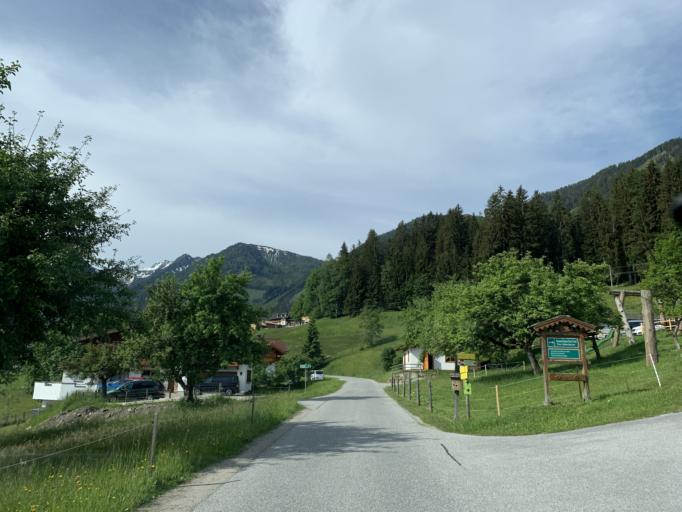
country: AT
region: Styria
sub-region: Politischer Bezirk Liezen
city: Schladming
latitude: 47.3700
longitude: 13.6670
